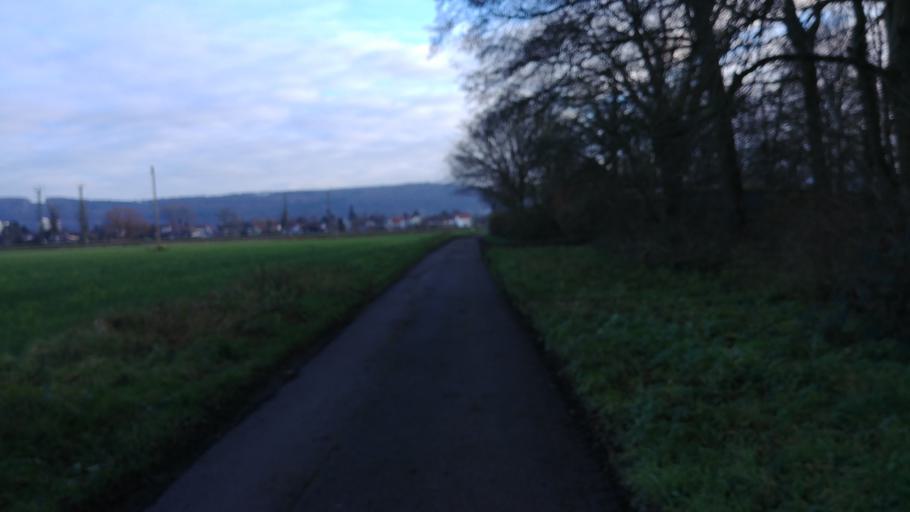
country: DE
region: Baden-Wuerttemberg
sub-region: Karlsruhe Region
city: Ettlingen
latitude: 48.9704
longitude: 8.3897
